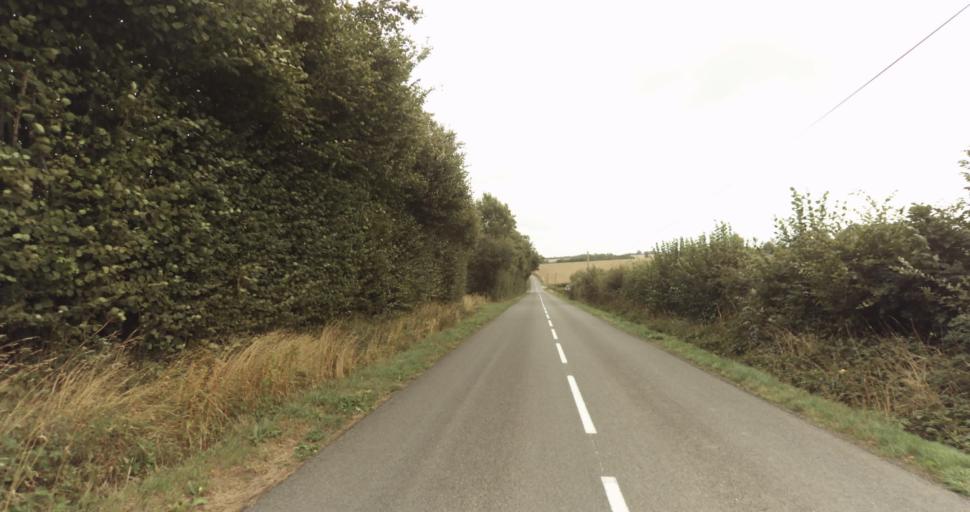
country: FR
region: Lower Normandy
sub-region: Departement de l'Orne
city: Gace
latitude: 48.8073
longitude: 0.3534
